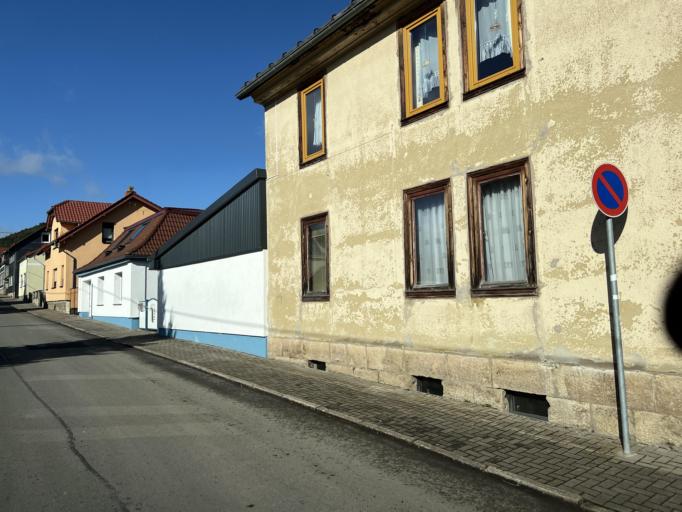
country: DE
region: Thuringia
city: Plaue
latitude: 50.7804
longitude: 10.9040
